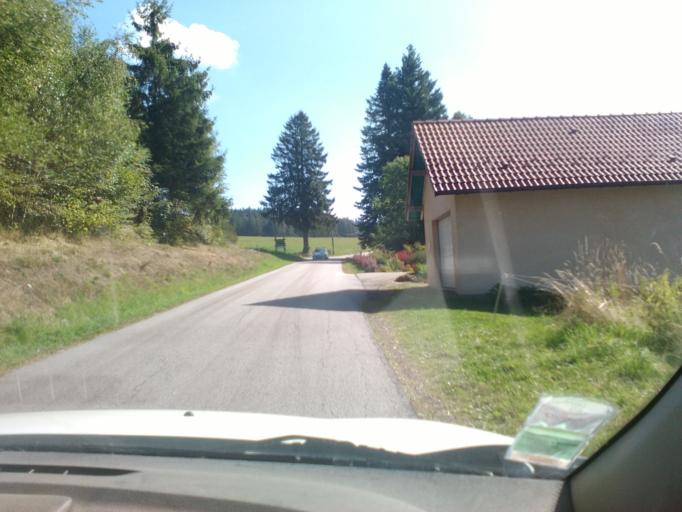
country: FR
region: Lorraine
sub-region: Departement des Vosges
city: Le Tholy
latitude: 48.0417
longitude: 6.7663
